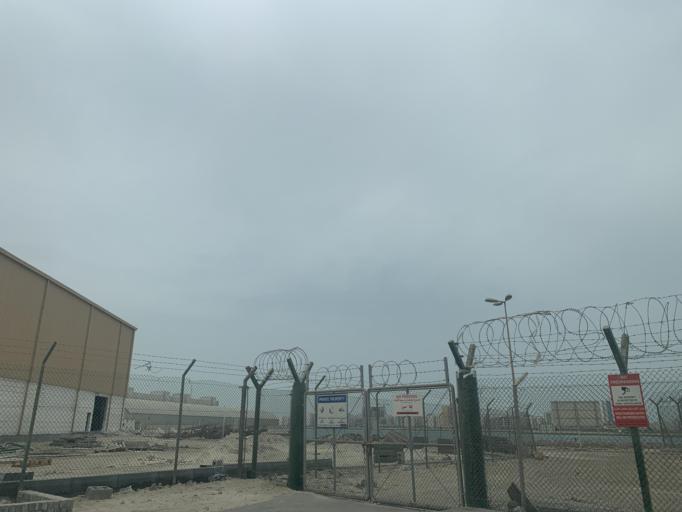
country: BH
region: Muharraq
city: Al Hadd
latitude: 26.2173
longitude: 50.6554
